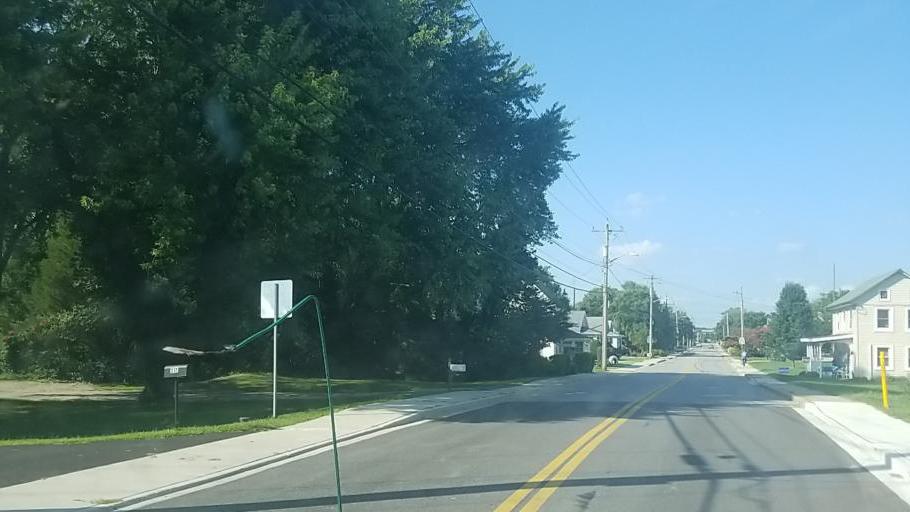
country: US
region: Maryland
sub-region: Worcester County
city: Berlin
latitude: 38.3282
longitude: -75.2165
